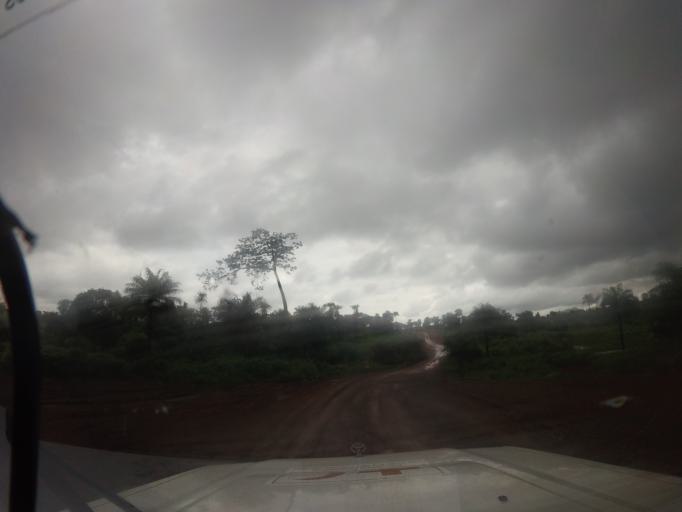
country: SL
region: Northern Province
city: Kamakwie
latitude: 9.3515
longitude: -12.2130
